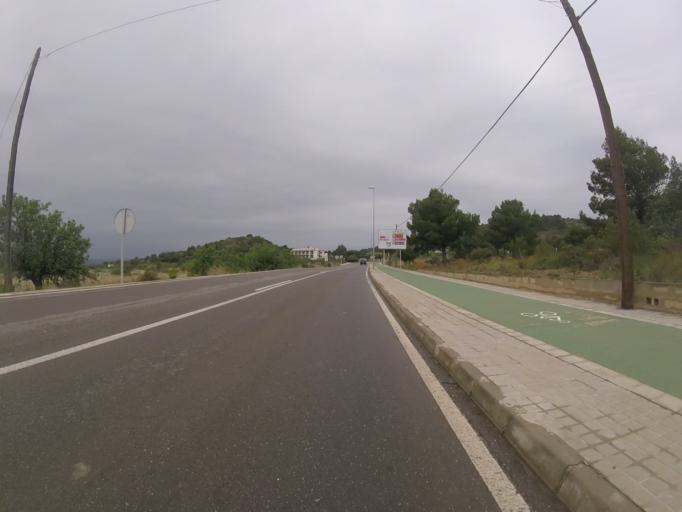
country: ES
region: Valencia
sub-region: Provincia de Castello
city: Alcoceber
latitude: 40.2479
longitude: 0.2554
